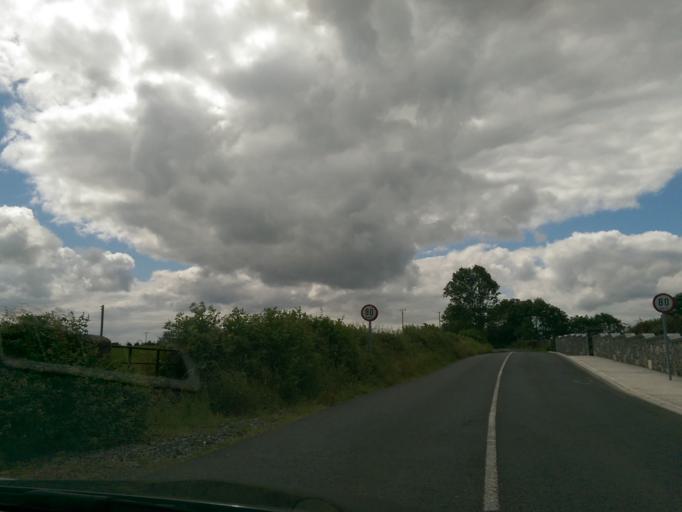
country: IE
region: Munster
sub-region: North Tipperary
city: Nenagh
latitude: 52.8499
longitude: -8.2071
